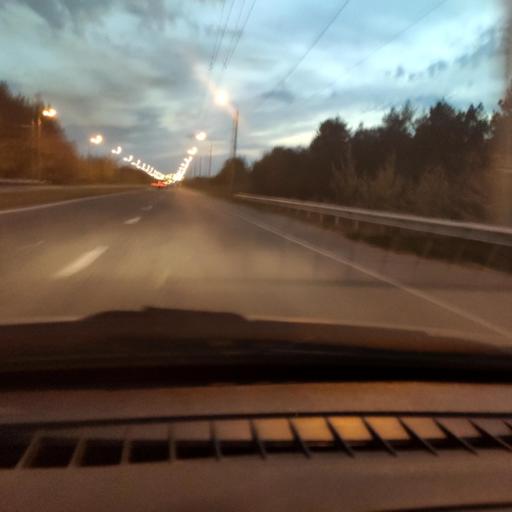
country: RU
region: Samara
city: Zhigulevsk
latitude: 53.5268
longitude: 49.5483
